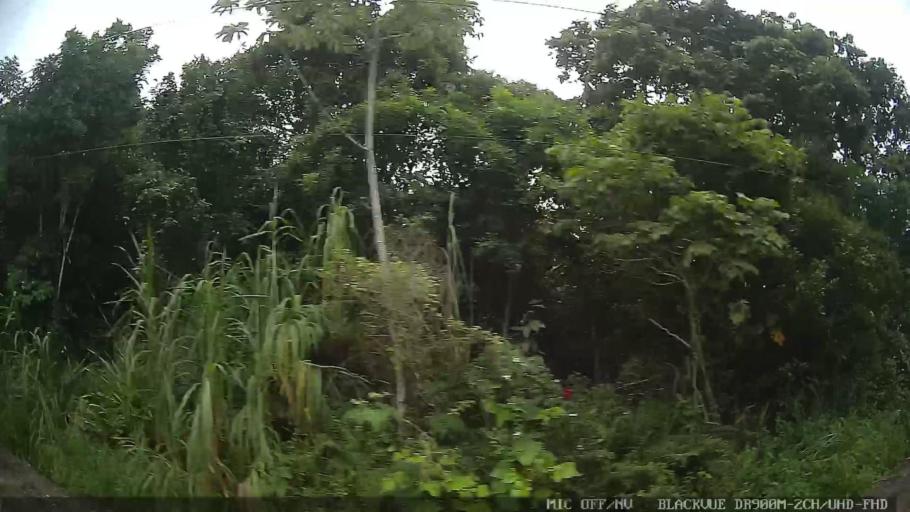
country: BR
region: Sao Paulo
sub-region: Iguape
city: Iguape
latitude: -24.6700
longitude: -47.4432
